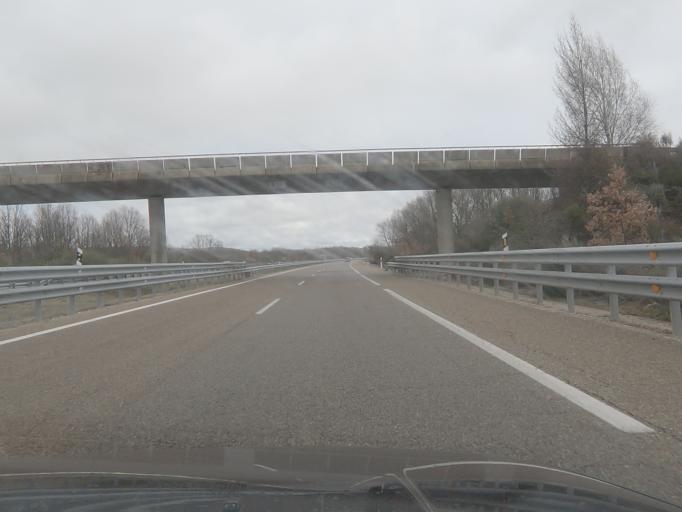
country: ES
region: Castille and Leon
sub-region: Provincia de Zamora
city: Cernadilla
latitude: 42.0381
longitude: -6.4459
